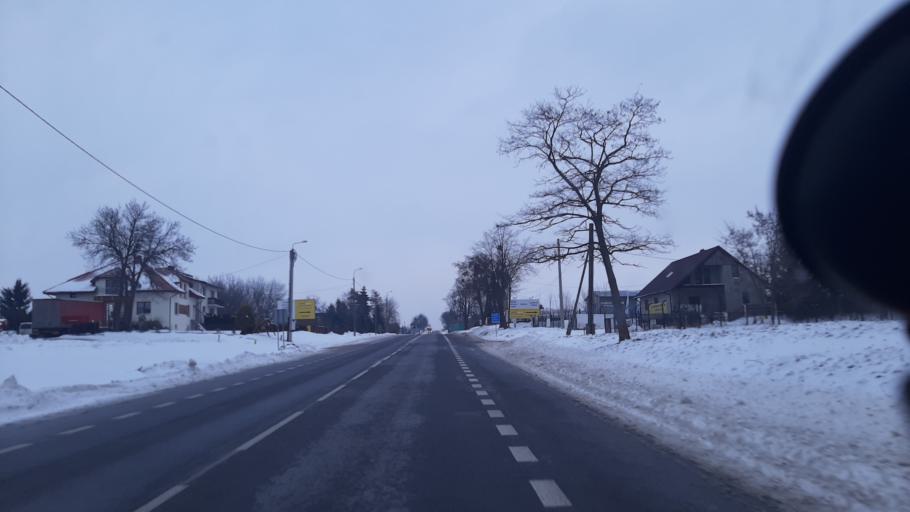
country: PL
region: Lublin Voivodeship
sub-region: Powiat pulawski
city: Markuszow
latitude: 51.3723
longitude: 22.2707
